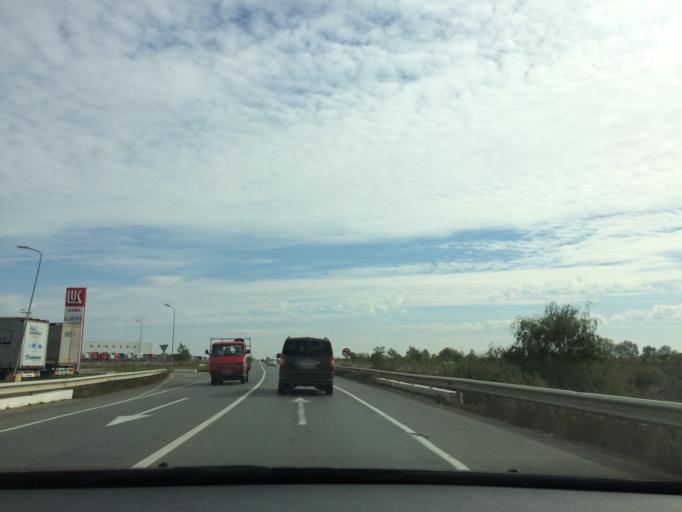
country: RO
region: Timis
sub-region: Comuna Dumbravita
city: Dumbravita
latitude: 45.8138
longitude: 21.2646
